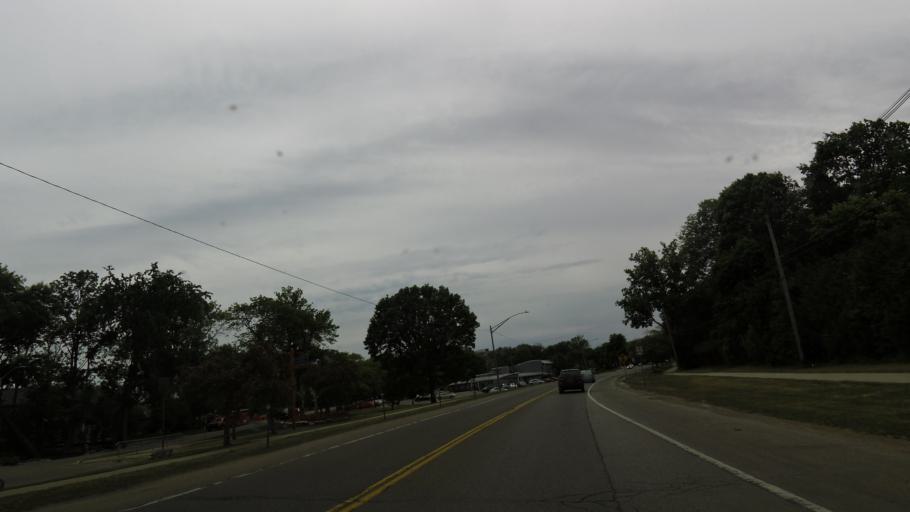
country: CA
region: Ontario
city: Oakville
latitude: 43.4061
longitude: -79.6956
